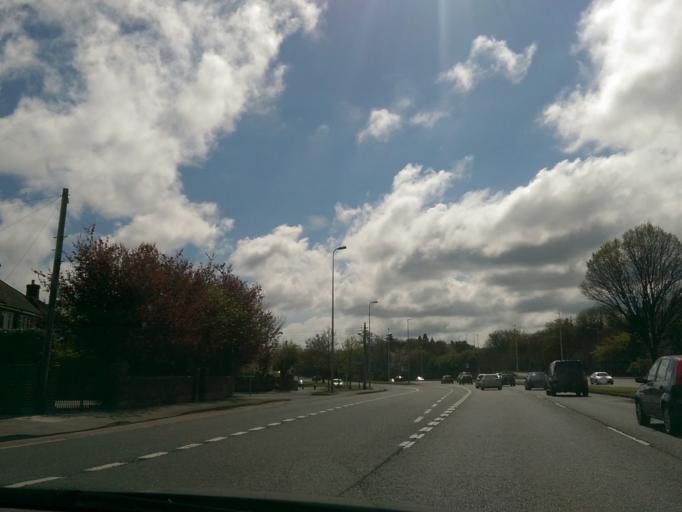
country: IE
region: Leinster
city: Donnybrook
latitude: 53.3115
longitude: -6.2206
